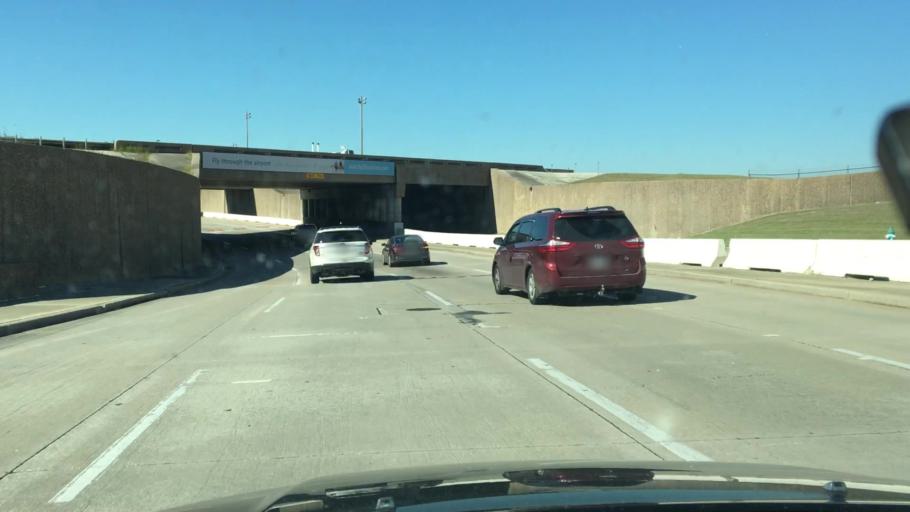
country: US
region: Texas
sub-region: Harris County
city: Humble
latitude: 29.9867
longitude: -95.3295
